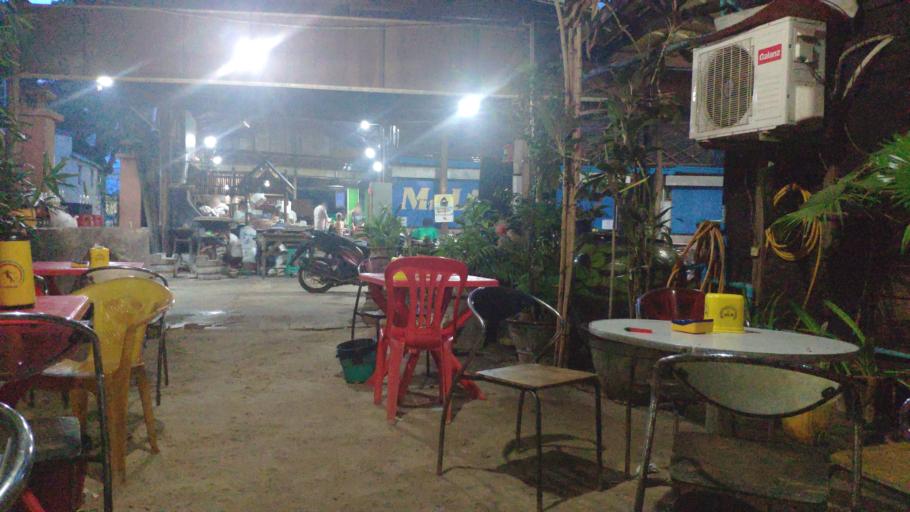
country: MM
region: Mandalay
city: Meiktila
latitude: 20.8775
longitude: 95.8444
